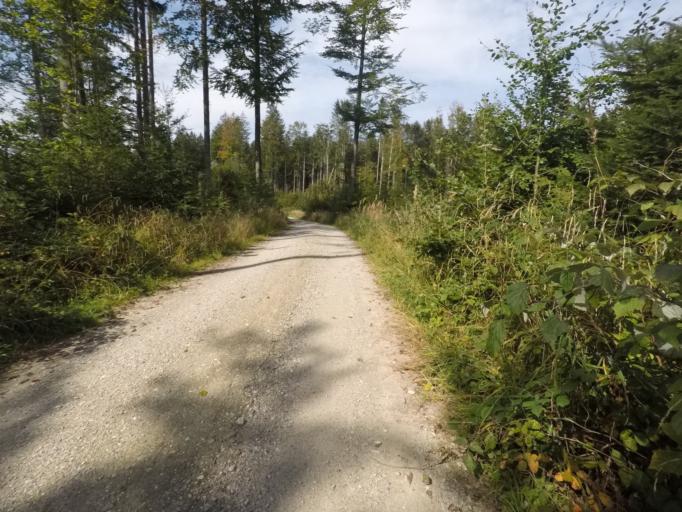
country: DE
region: Bavaria
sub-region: Upper Bavaria
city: Geretsried
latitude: 47.8462
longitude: 11.5061
